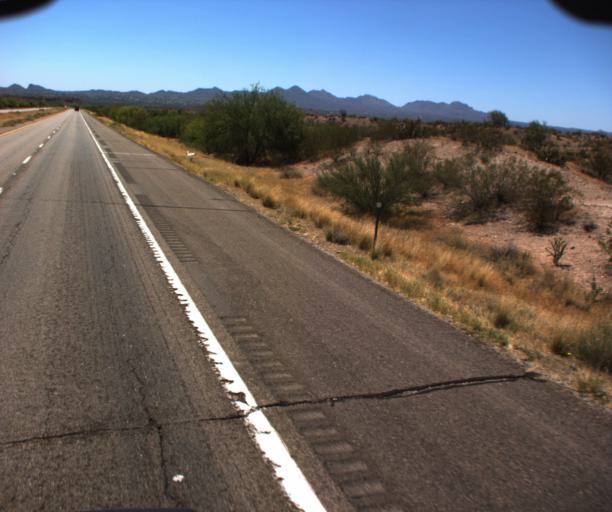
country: US
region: Arizona
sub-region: Maricopa County
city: Fountain Hills
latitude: 33.5811
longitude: -111.6320
